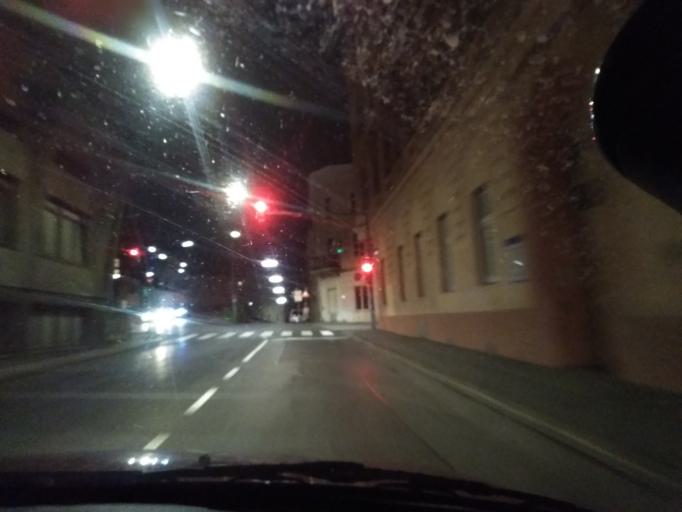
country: AT
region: Vienna
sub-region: Wien Stadt
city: Vienna
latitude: 48.1935
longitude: 16.3292
